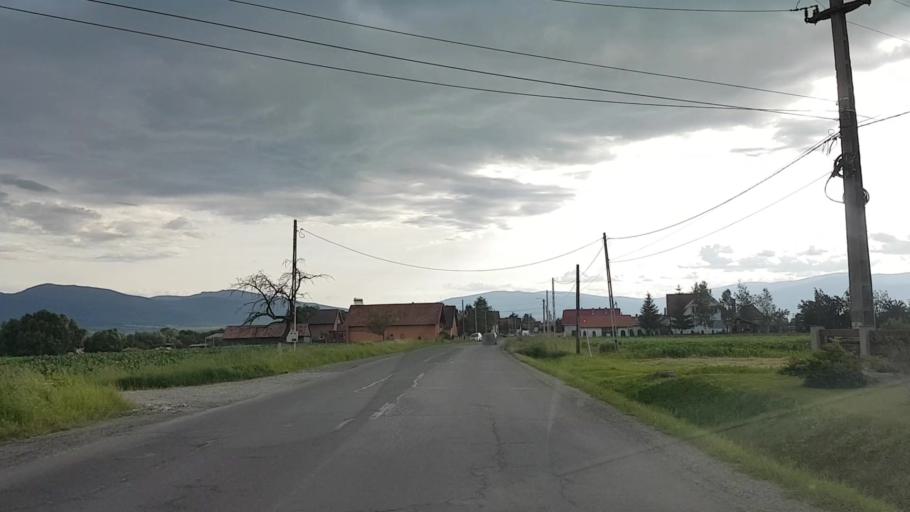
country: RO
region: Harghita
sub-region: Comuna Ciumani
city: Ciumani
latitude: 46.7067
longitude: 25.5291
